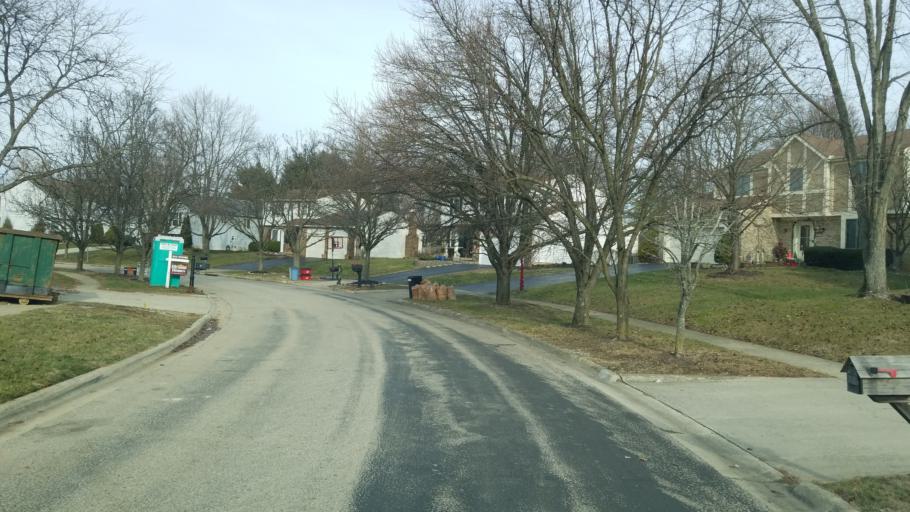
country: US
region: Ohio
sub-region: Delaware County
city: Lewis Center
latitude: 40.1593
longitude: -83.0273
